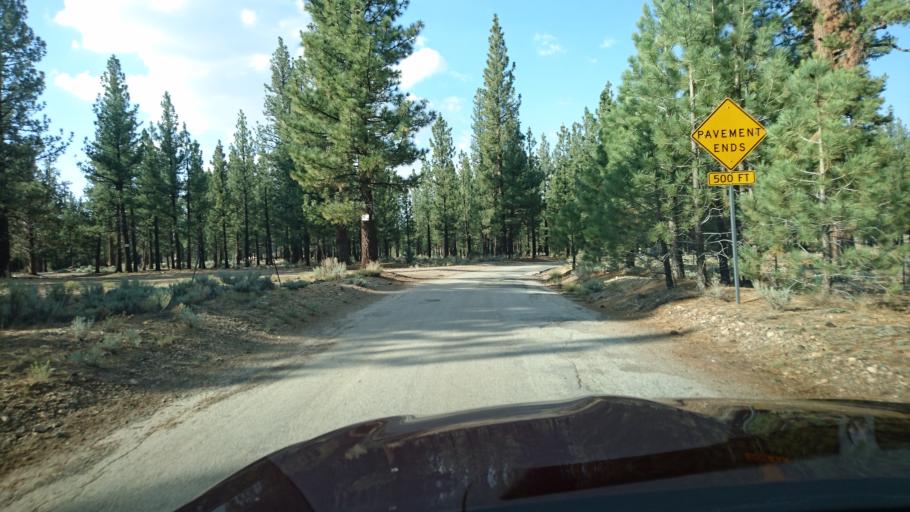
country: US
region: California
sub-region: San Bernardino County
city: Big Bear City
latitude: 34.2490
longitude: -116.8105
